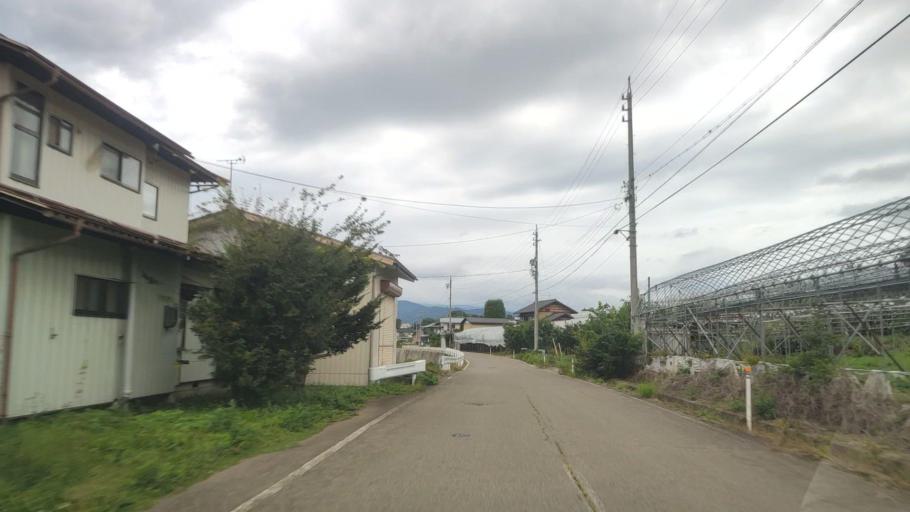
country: JP
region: Nagano
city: Nakano
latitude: 36.7789
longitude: 138.3751
